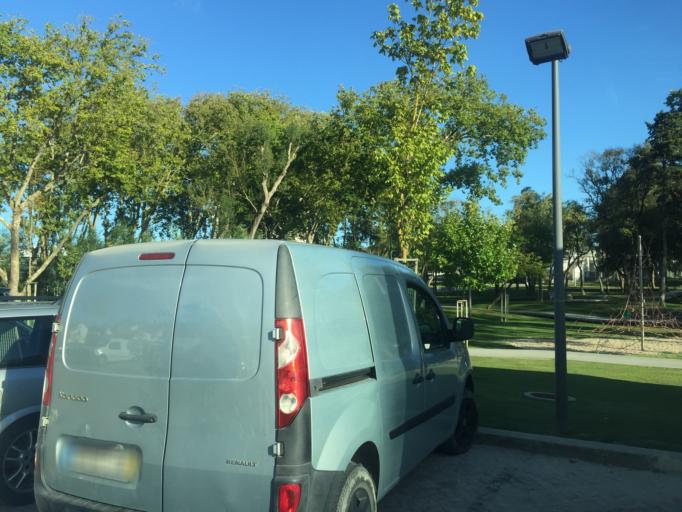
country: PT
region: Lisbon
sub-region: Torres Vedras
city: Torres Vedras
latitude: 39.0980
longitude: -9.2615
